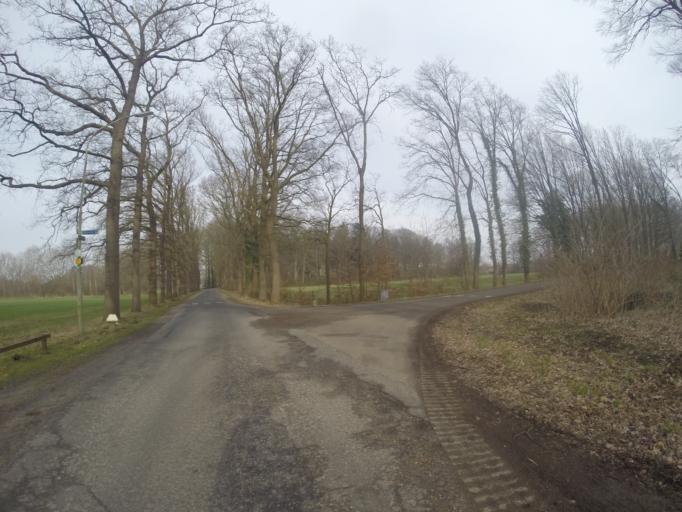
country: NL
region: Gelderland
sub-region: Gemeente Lochem
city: Almen
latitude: 52.1093
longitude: 6.2866
